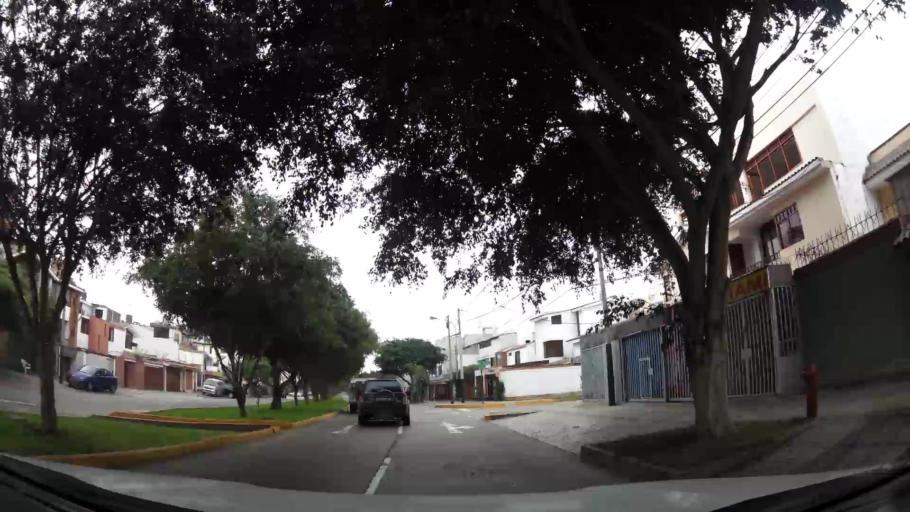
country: PE
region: Lima
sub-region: Lima
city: Surco
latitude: -12.1323
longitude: -76.9864
